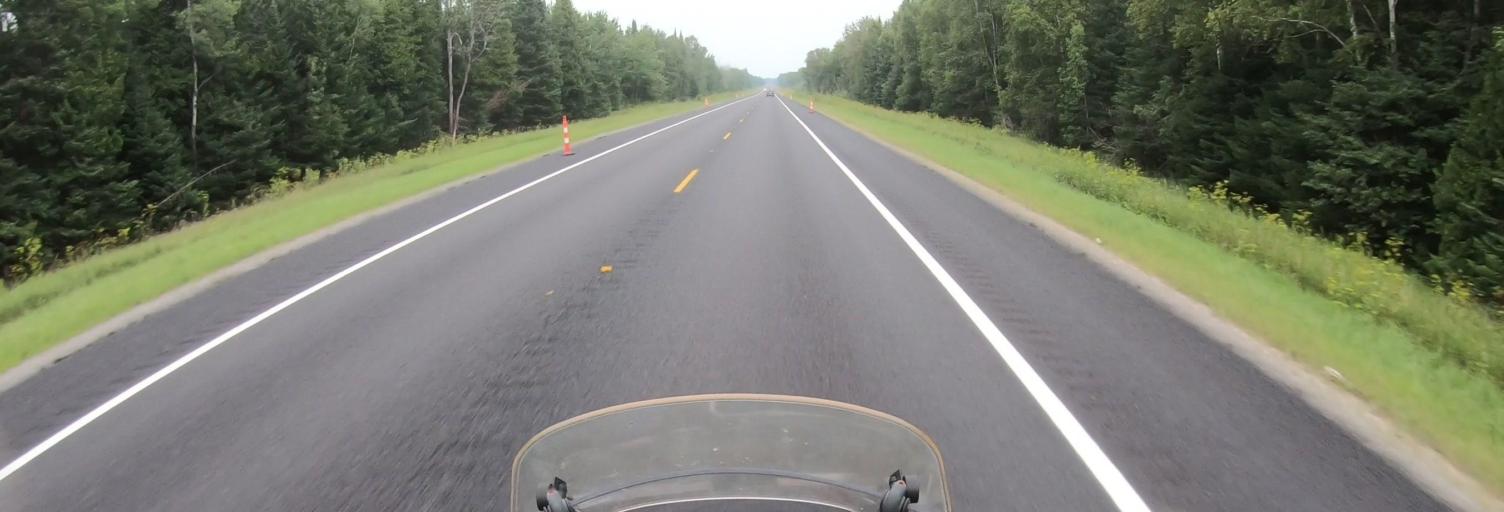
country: US
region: Michigan
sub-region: Mackinac County
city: Saint Ignace
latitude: 45.7174
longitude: -84.7507
